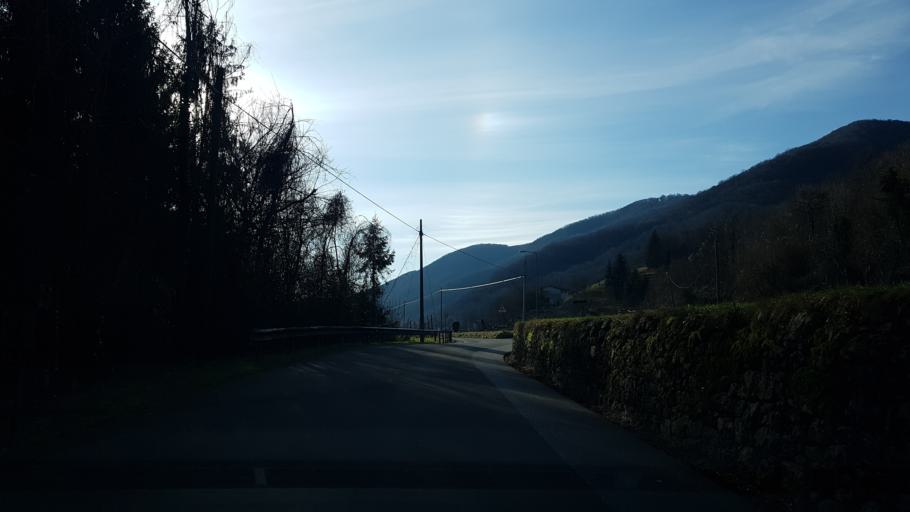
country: IT
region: Friuli Venezia Giulia
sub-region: Provincia di Udine
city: Stregna
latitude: 46.1485
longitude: 13.5610
